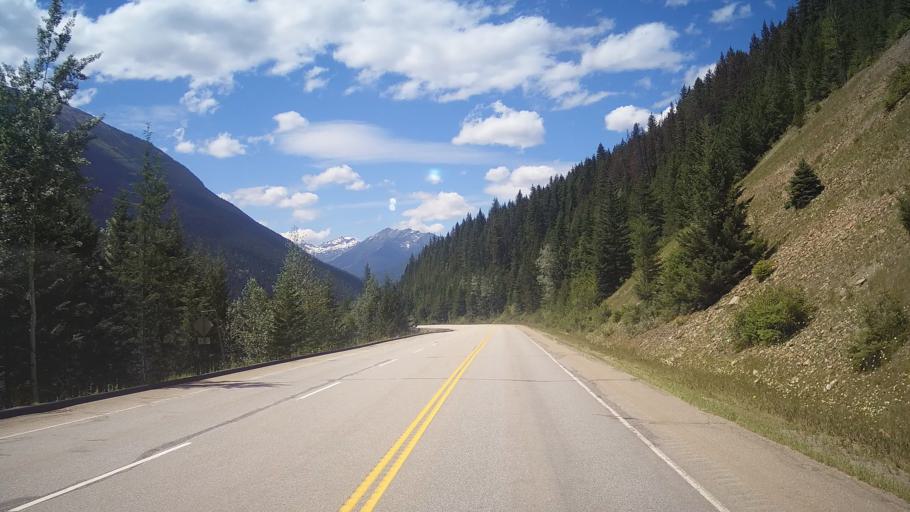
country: CA
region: Alberta
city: Grande Cache
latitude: 53.0200
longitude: -119.1268
